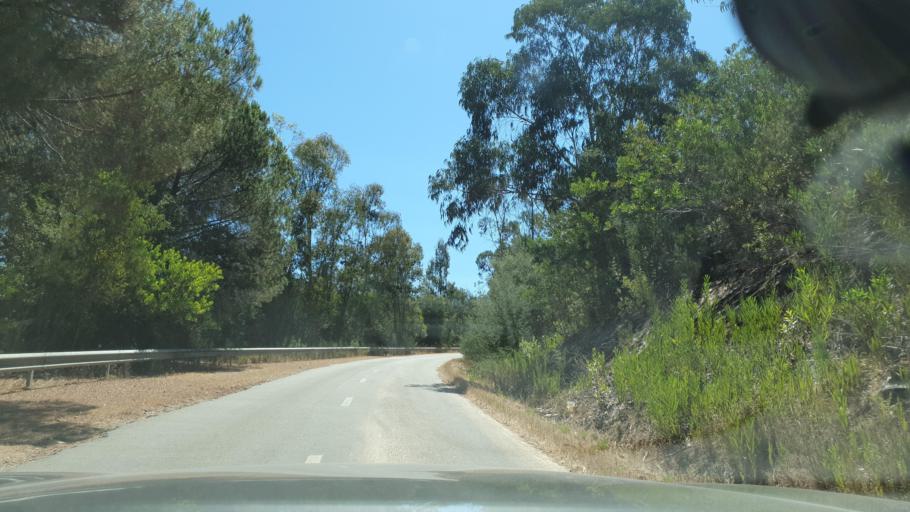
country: PT
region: Beja
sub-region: Odemira
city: Odemira
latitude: 37.5072
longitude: -8.4400
